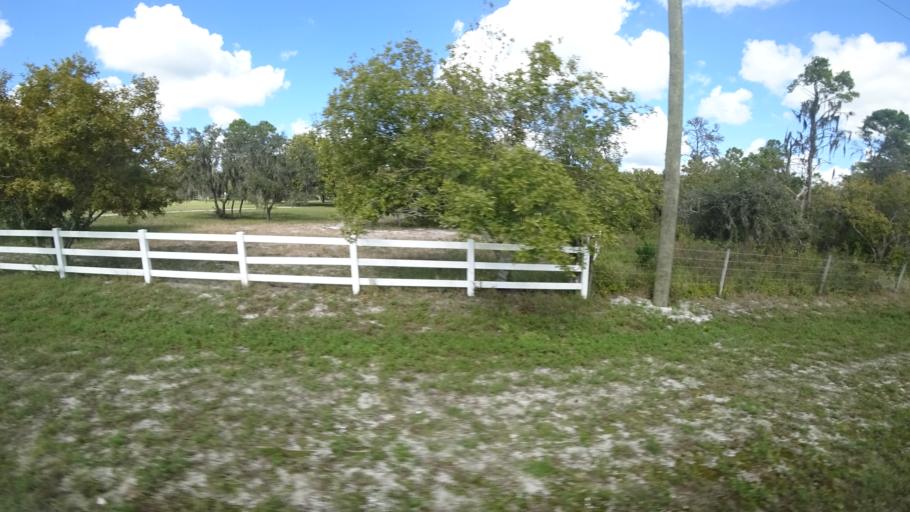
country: US
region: Florida
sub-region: Sarasota County
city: Lake Sarasota
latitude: 27.3528
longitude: -82.2356
